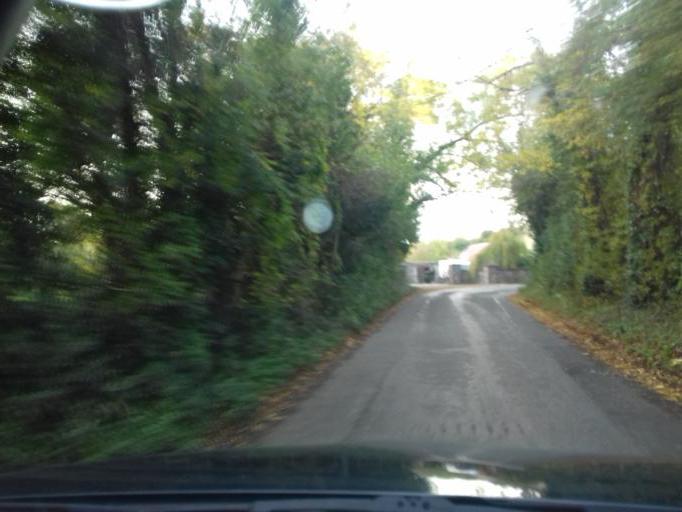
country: IE
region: Leinster
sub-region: An Mhi
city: Dunboyne
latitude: 53.3856
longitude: -6.4617
